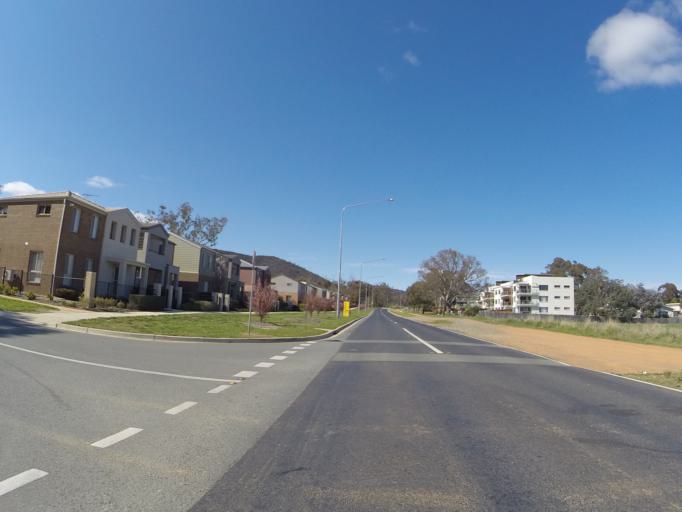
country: AU
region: Australian Capital Territory
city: Kaleen
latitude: -35.2258
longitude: 149.1657
